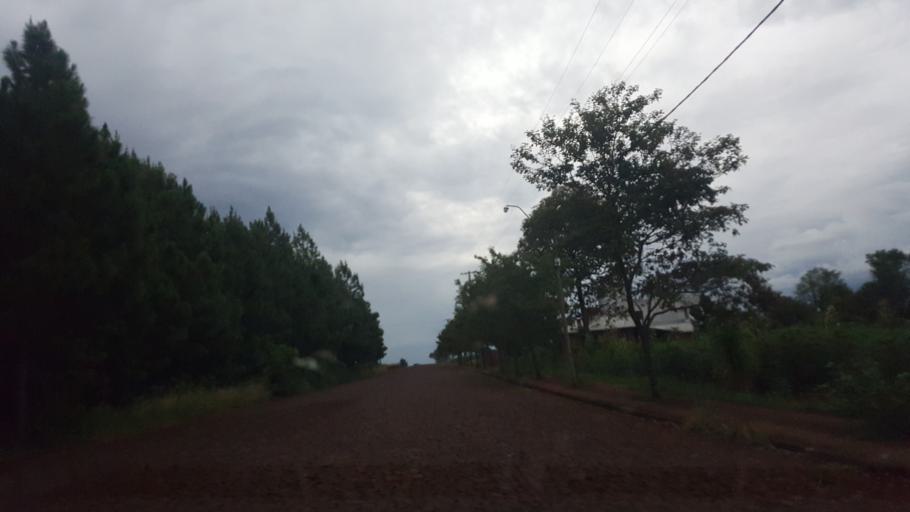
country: AR
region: Misiones
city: Capiovi
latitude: -26.9349
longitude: -55.0461
